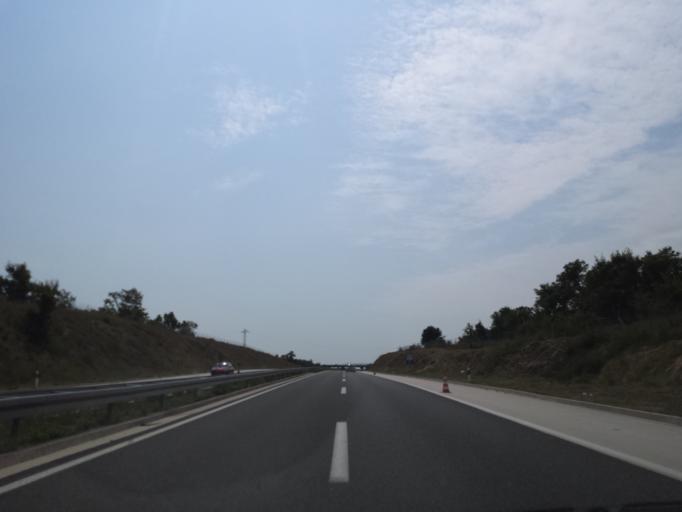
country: HR
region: Zadarska
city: Posedarje
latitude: 44.2066
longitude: 15.4449
